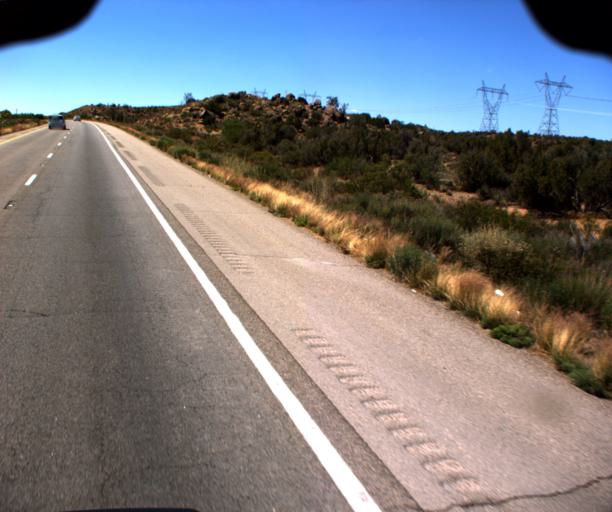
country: US
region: Arizona
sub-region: Yavapai County
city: Bagdad
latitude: 34.4716
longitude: -113.3173
